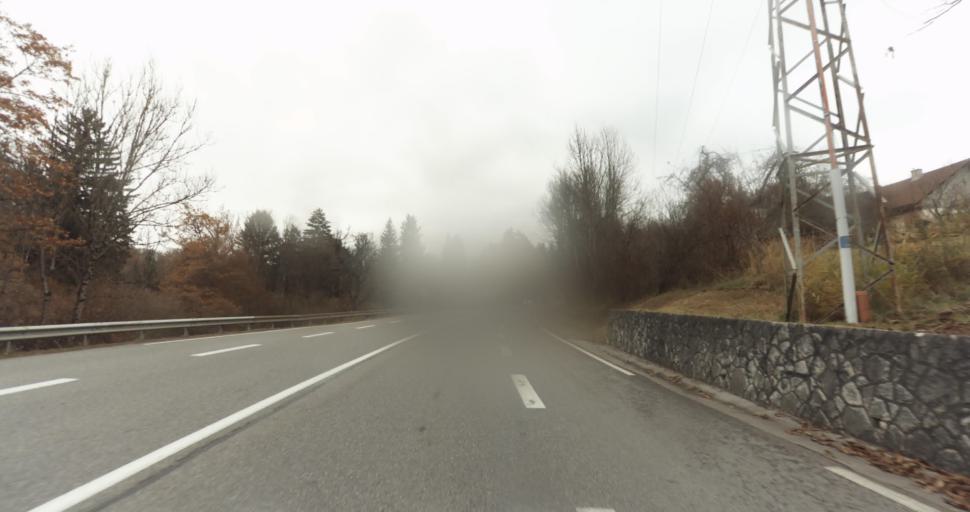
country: FR
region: Rhone-Alpes
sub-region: Departement de la Haute-Savoie
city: Groisy
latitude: 46.0044
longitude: 6.1892
